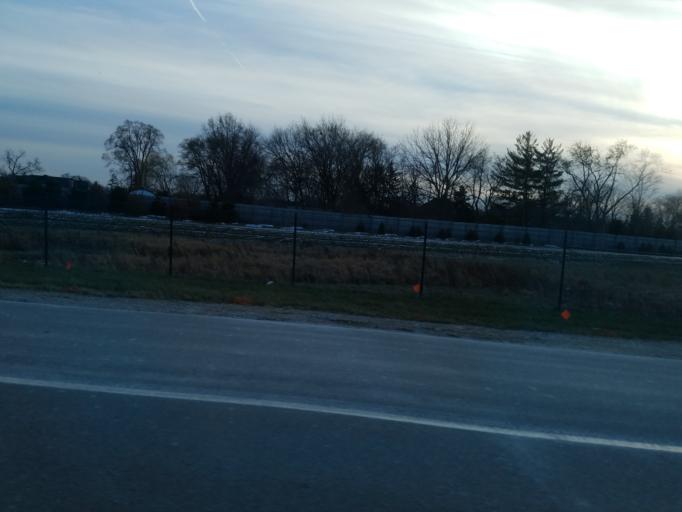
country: US
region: Illinois
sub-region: DuPage County
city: Itasca
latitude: 41.9826
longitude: -87.9998
